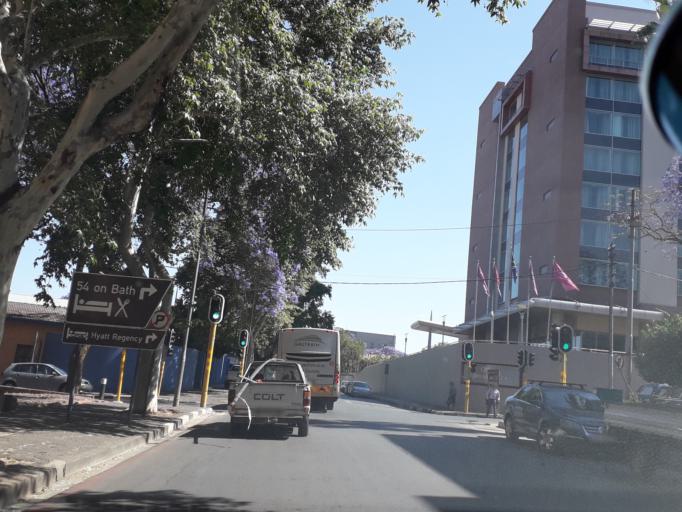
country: ZA
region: Gauteng
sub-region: City of Johannesburg Metropolitan Municipality
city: Johannesburg
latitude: -26.1459
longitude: 28.0388
